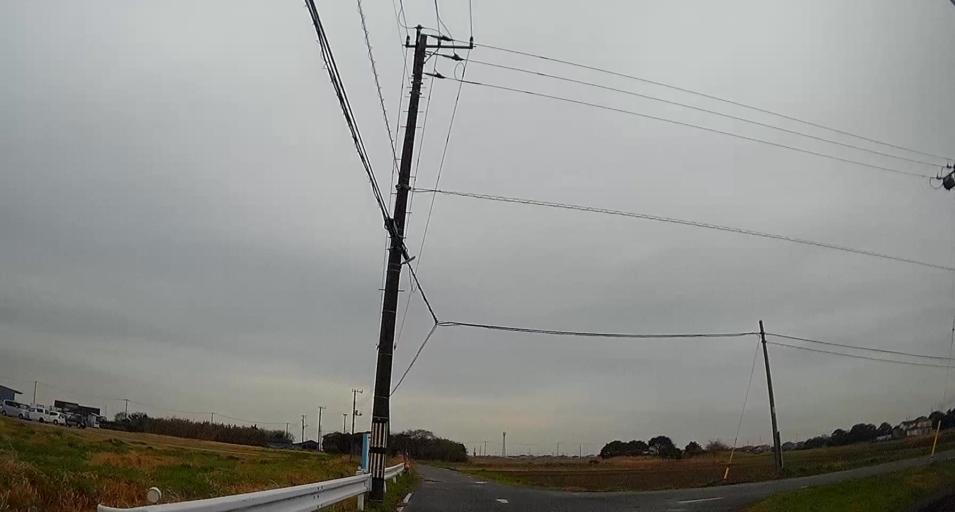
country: JP
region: Chiba
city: Kisarazu
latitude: 35.4222
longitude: 139.9024
